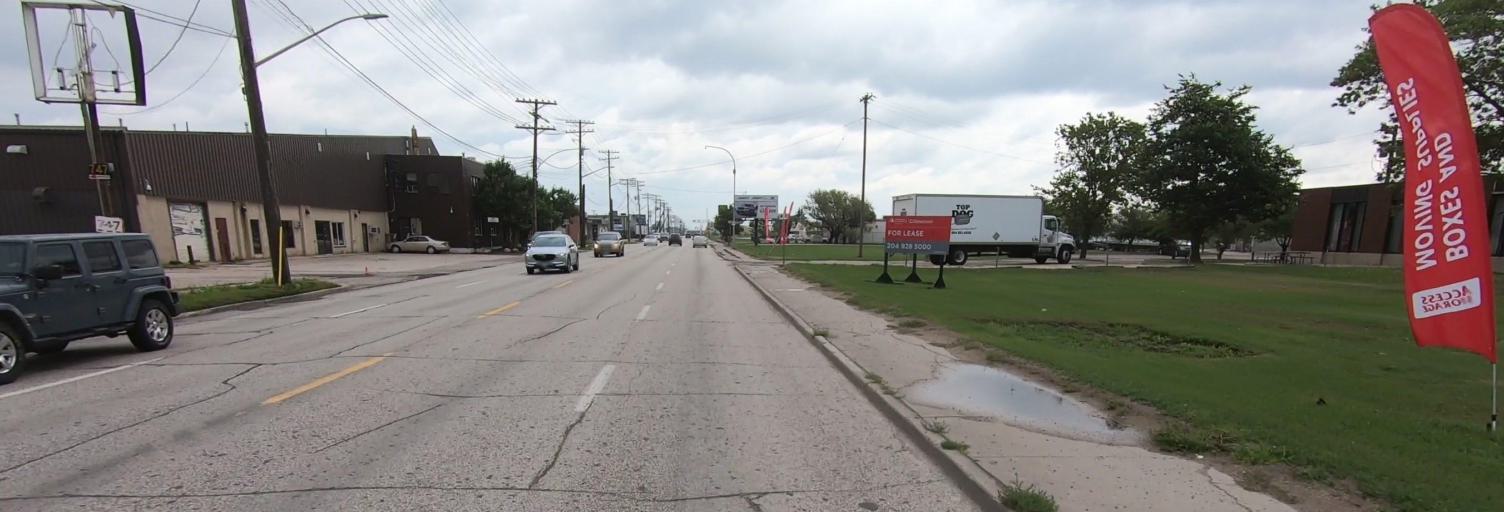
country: CA
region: Manitoba
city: Winnipeg
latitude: 49.8819
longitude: -97.0907
